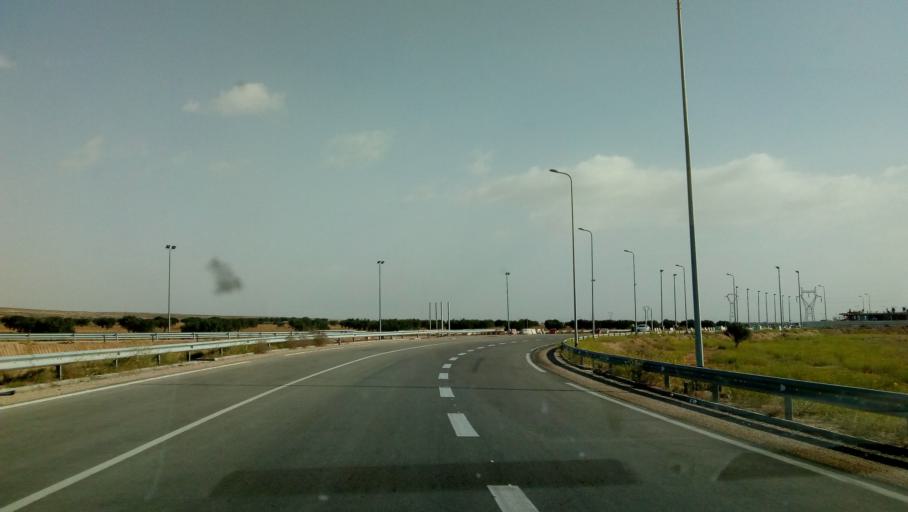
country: TN
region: Qabis
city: Gabes
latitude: 33.8830
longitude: 9.9976
